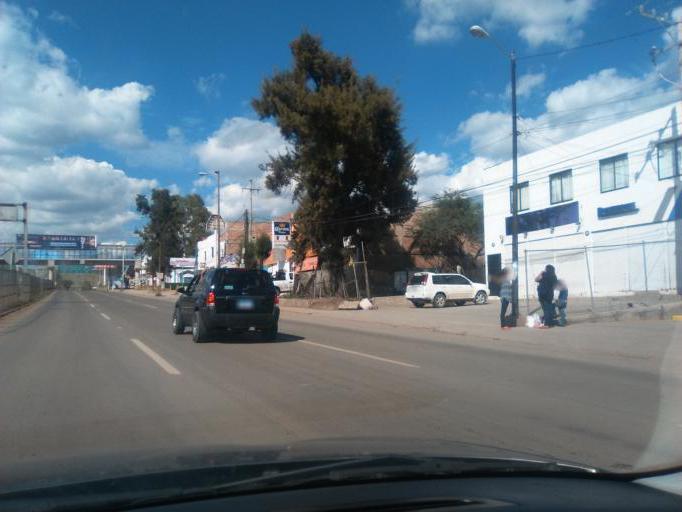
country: MX
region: Guanajuato
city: Marfil
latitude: 20.9884
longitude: -101.2851
